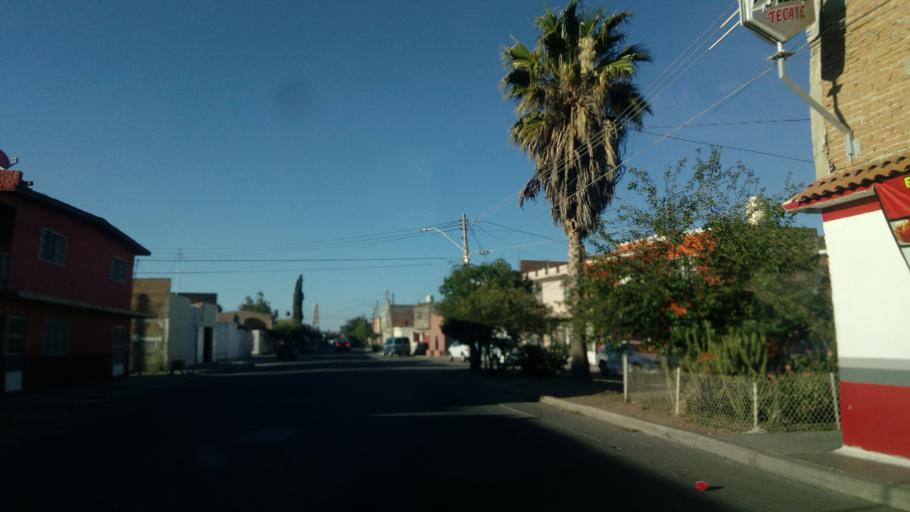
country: MX
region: Durango
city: Victoria de Durango
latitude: 23.9982
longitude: -104.6754
